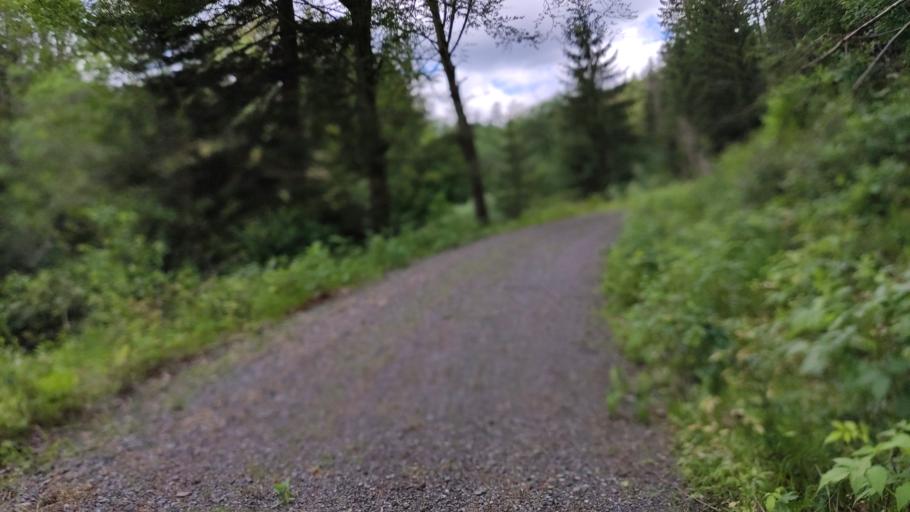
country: DE
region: Bavaria
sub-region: Upper Franconia
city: Tschirn
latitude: 50.3755
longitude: 11.4676
